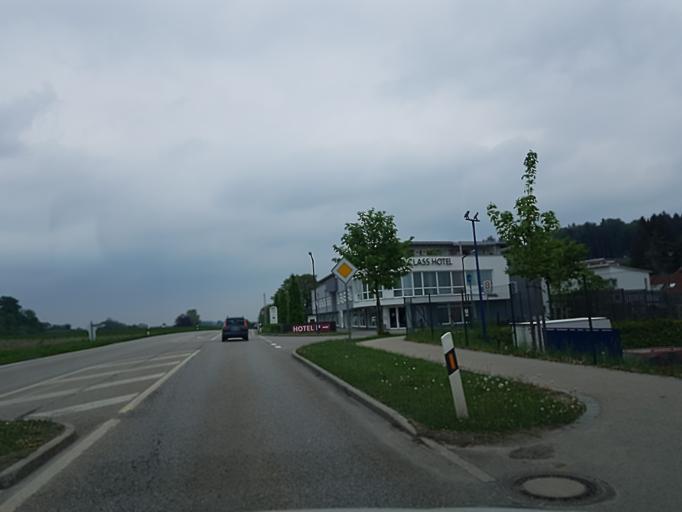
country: DE
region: Bavaria
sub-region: Upper Bavaria
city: Ebersberg
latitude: 48.0949
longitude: 11.9647
